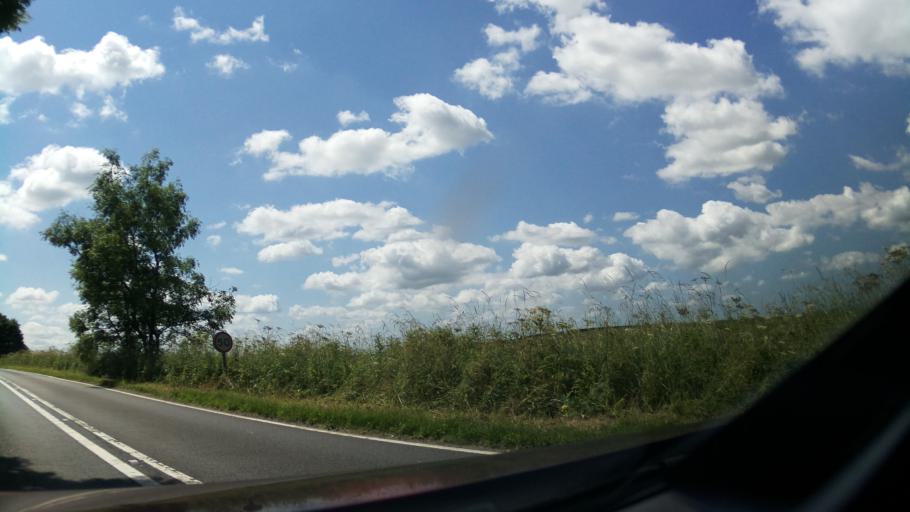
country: GB
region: England
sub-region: Derbyshire
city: Ashbourne
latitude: 53.1134
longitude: -1.7548
